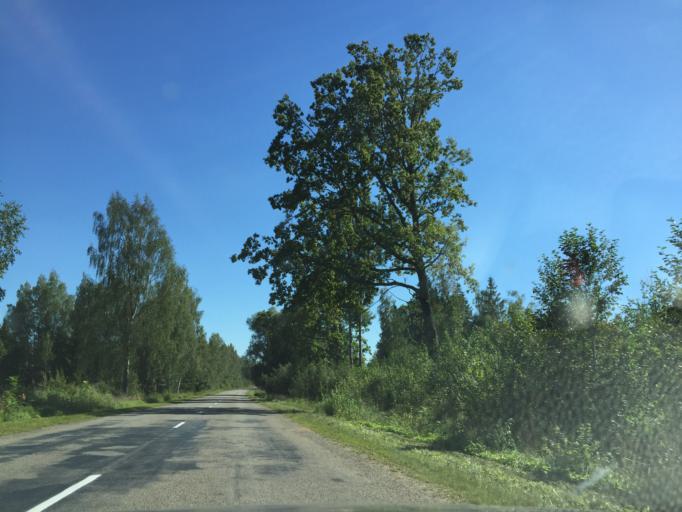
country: LV
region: Akniste
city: Akniste
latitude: 56.0750
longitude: 25.8852
